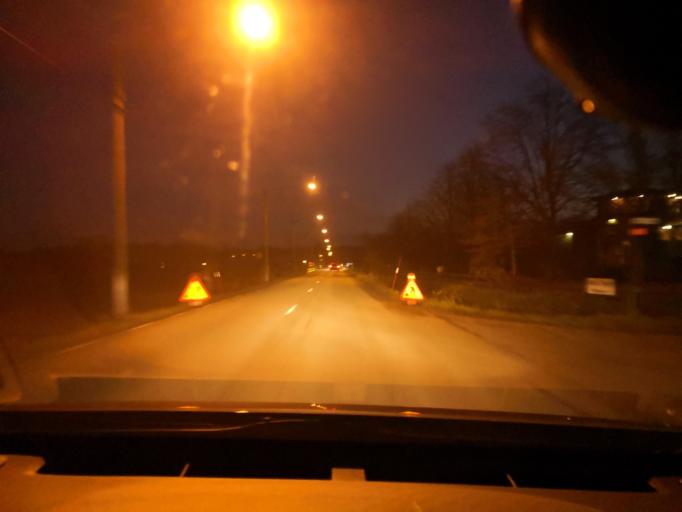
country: SE
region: OErebro
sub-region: Orebro Kommun
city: Orebro
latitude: 59.2605
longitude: 15.2729
